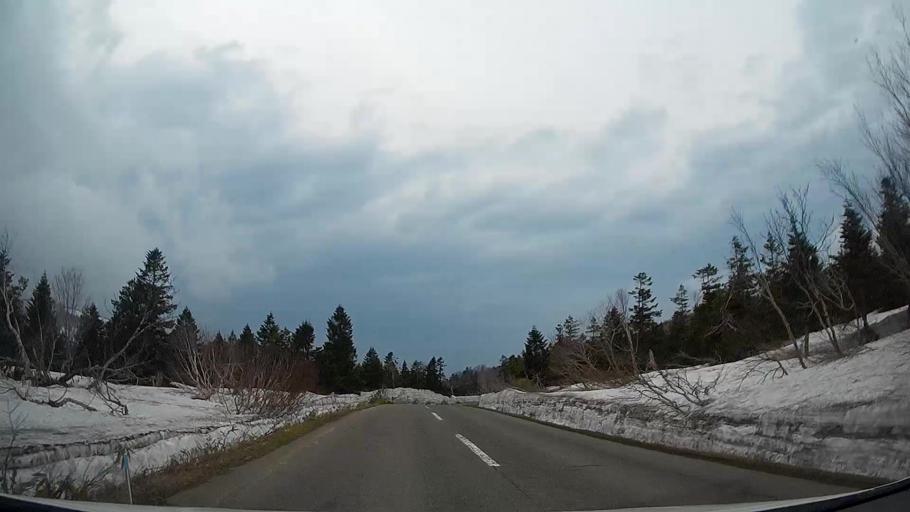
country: JP
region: Aomori
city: Aomori Shi
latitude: 40.6375
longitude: 140.8666
